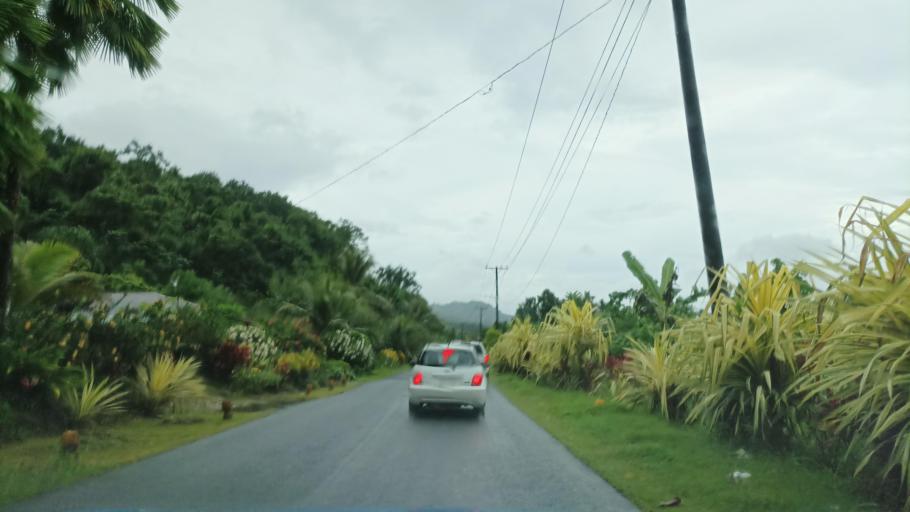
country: FM
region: Pohnpei
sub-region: Kolonia Municipality
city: Kolonia Town
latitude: 6.9494
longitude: 158.1892
